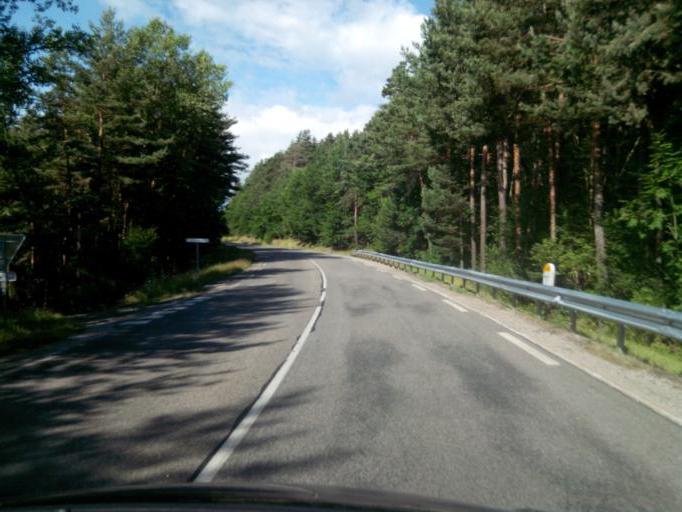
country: FR
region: Auvergne
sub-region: Departement de la Haute-Loire
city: Beauzac
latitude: 45.2425
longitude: 4.0809
